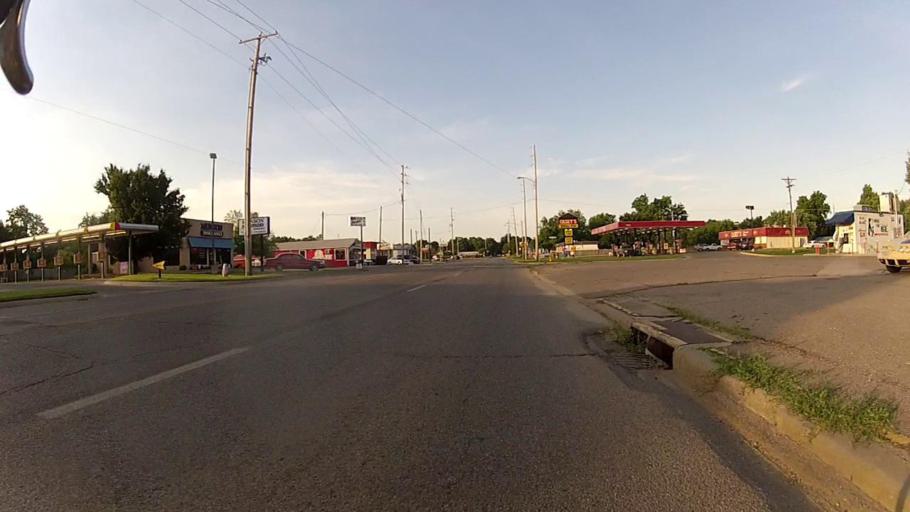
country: US
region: Kansas
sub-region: Cowley County
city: Arkansas City
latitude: 37.0802
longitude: -97.0401
